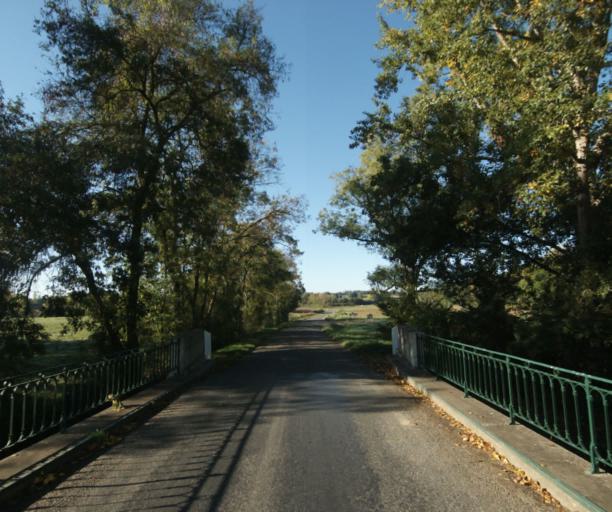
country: FR
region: Midi-Pyrenees
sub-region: Departement du Gers
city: Gondrin
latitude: 43.8468
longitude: 0.2418
